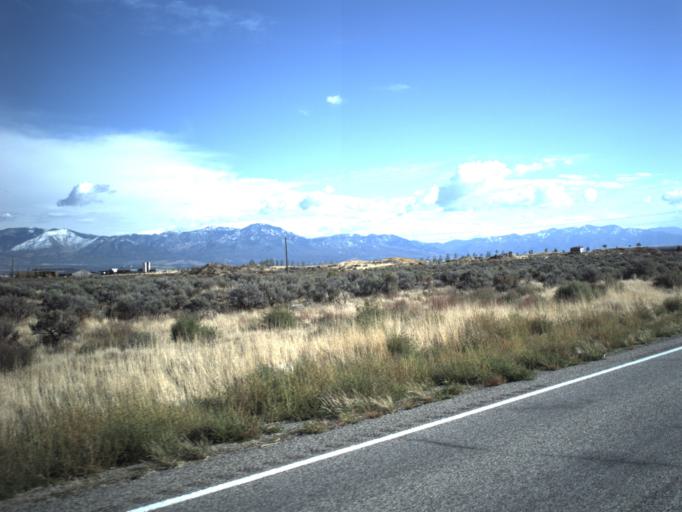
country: US
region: Utah
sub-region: Millard County
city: Fillmore
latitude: 39.1787
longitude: -112.4101
